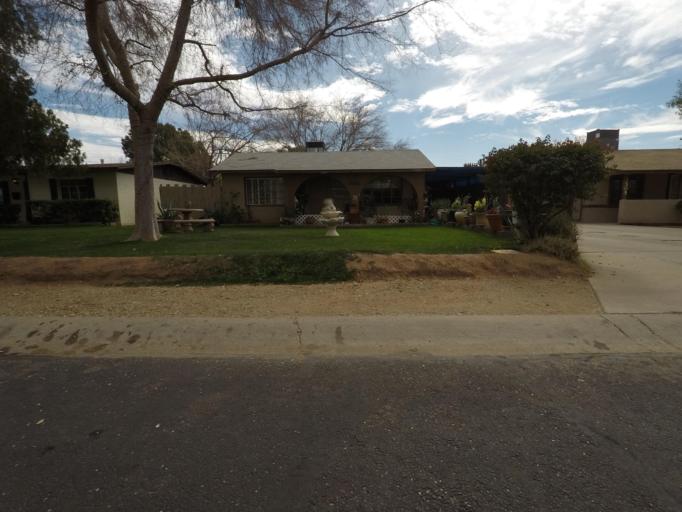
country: US
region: Arizona
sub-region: Maricopa County
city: Phoenix
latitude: 33.4768
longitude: -112.0060
